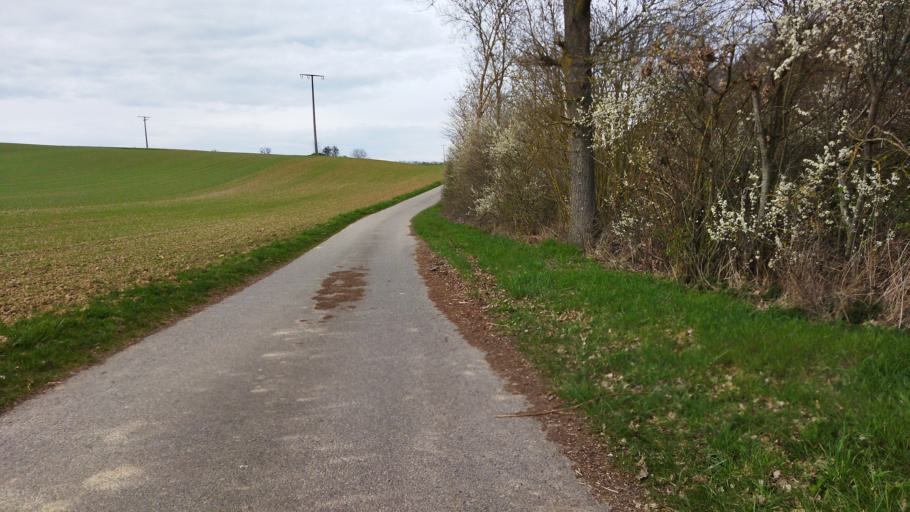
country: DE
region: Baden-Wuerttemberg
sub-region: Regierungsbezirk Stuttgart
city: Gundelsheim
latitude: 49.2812
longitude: 9.1861
